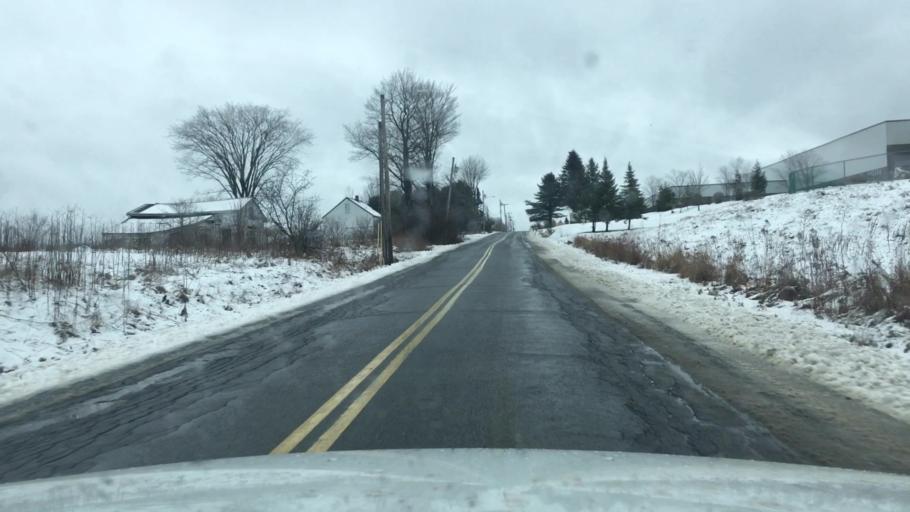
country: US
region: Maine
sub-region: Knox County
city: Rockland
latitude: 44.0901
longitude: -69.1287
